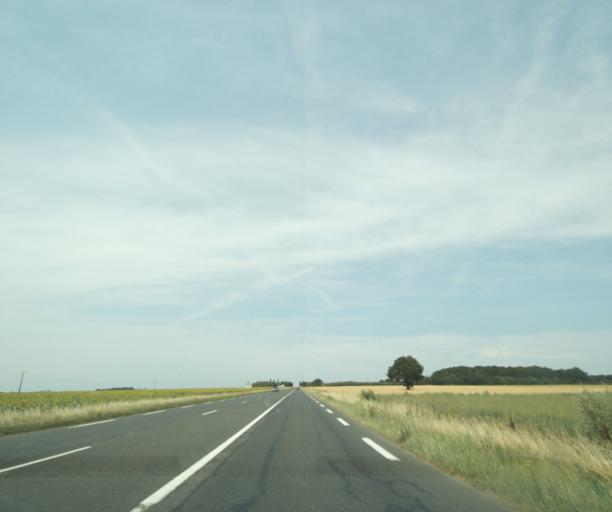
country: FR
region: Centre
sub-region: Departement d'Indre-et-Loire
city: Sainte-Maure-de-Touraine
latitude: 47.1655
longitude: 0.6508
